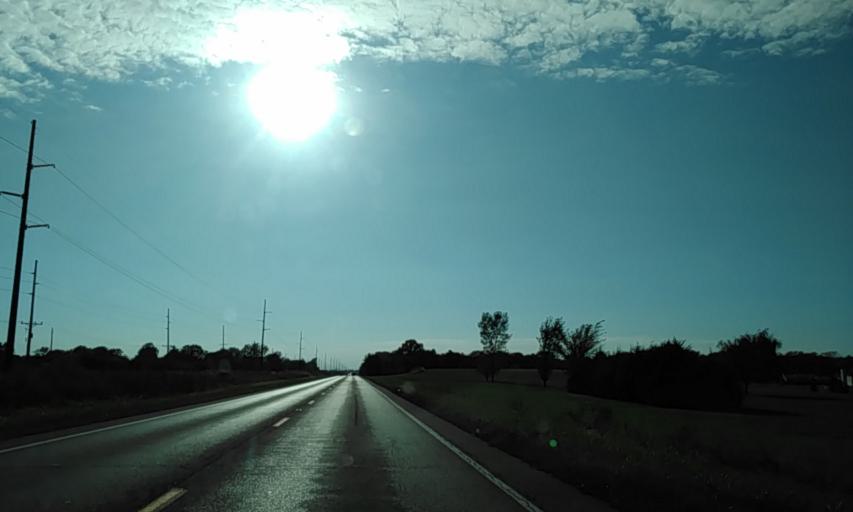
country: US
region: Illinois
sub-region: Madison County
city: Highland
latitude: 38.7362
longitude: -89.7079
